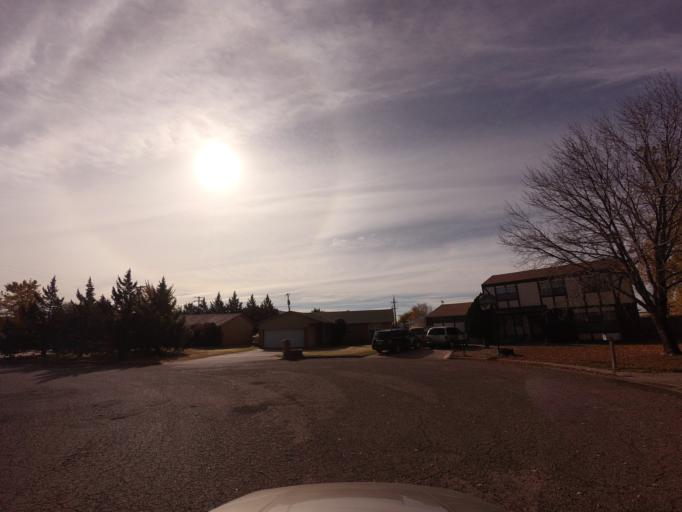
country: US
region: New Mexico
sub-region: Curry County
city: Clovis
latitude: 34.4203
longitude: -103.2290
